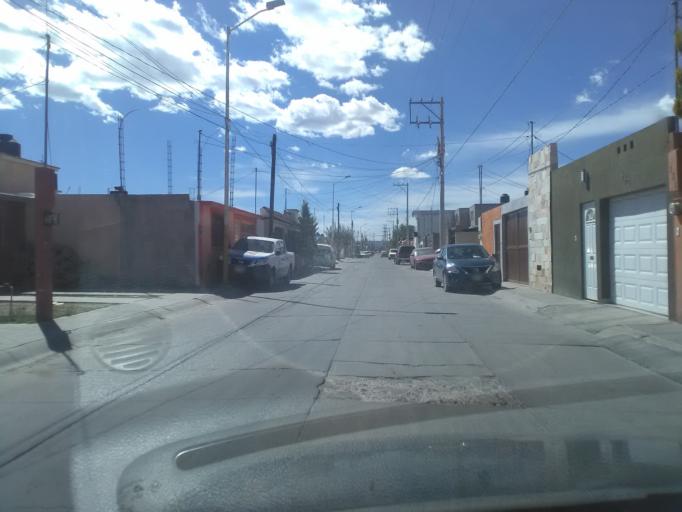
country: MX
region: Durango
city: Victoria de Durango
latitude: 24.0047
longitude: -104.6288
